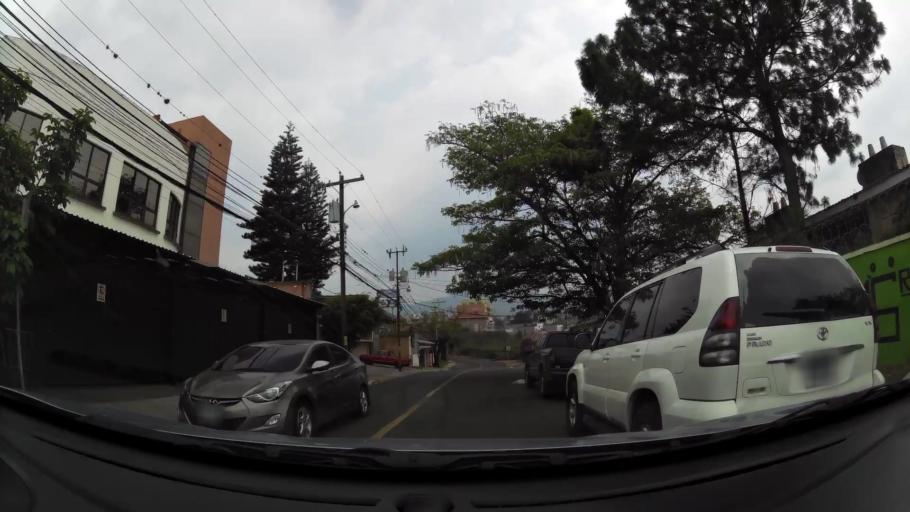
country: HN
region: Francisco Morazan
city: Tegucigalpa
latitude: 14.0832
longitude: -87.1746
